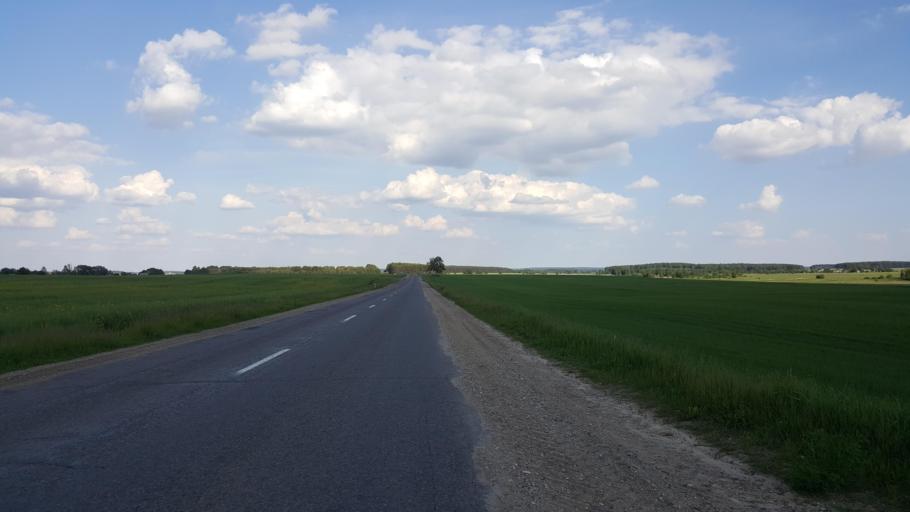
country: BY
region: Brest
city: Kamyanyets
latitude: 52.4127
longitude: 23.7158
